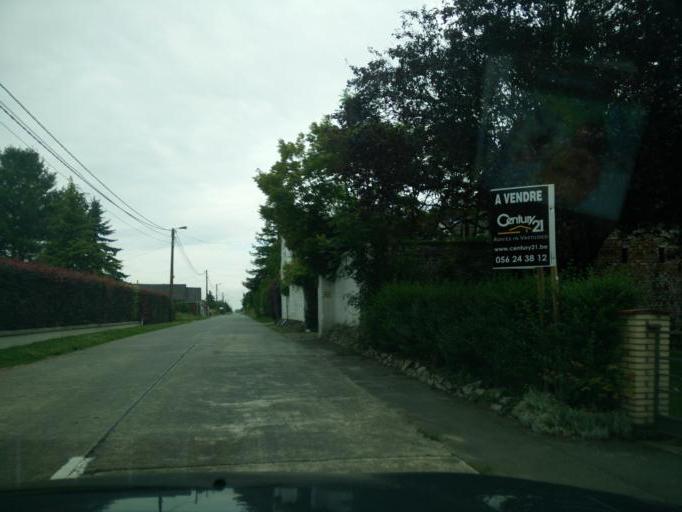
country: BE
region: Wallonia
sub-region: Province du Hainaut
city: Flobecq
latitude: 50.7564
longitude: 3.7280
